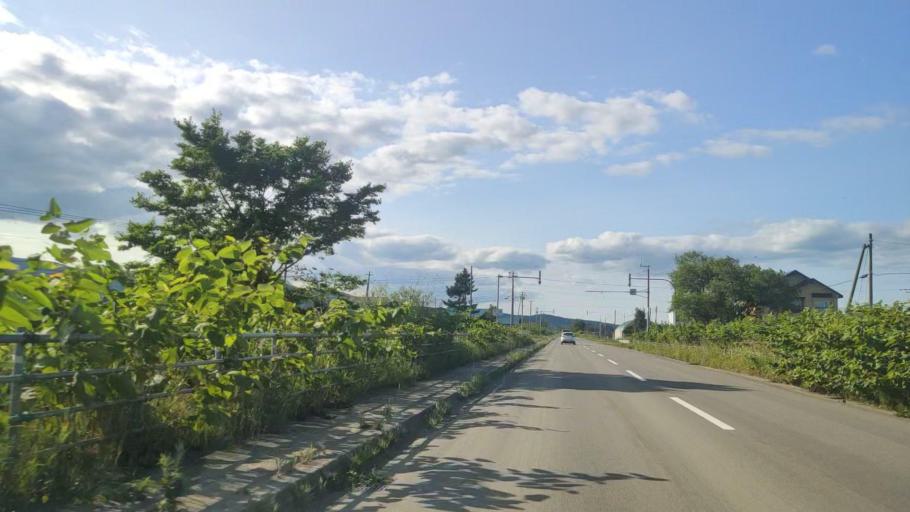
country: JP
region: Hokkaido
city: Makubetsu
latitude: 44.8232
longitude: 142.0653
